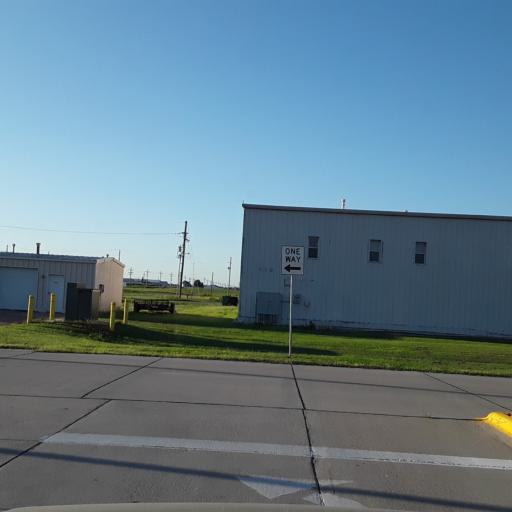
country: US
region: Nebraska
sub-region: Hall County
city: Grand Island
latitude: 40.9706
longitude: -98.3196
